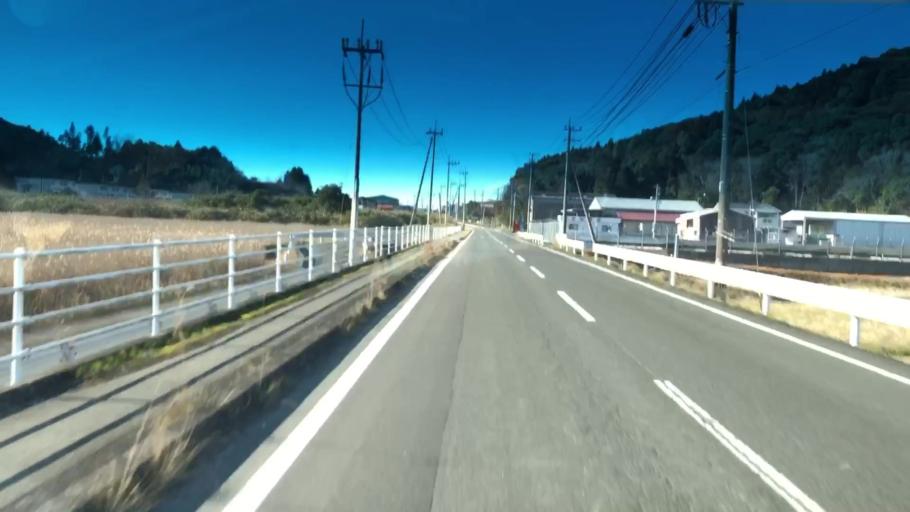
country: JP
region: Kagoshima
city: Satsumasendai
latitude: 31.8186
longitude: 130.2674
